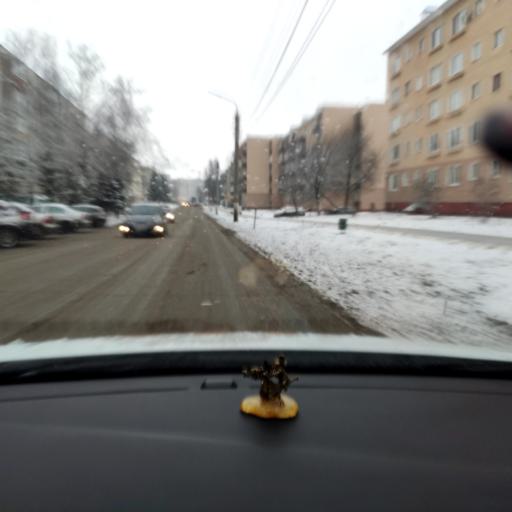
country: RU
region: Tatarstan
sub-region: Zelenodol'skiy Rayon
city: Zelenodolsk
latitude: 55.8510
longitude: 48.5251
